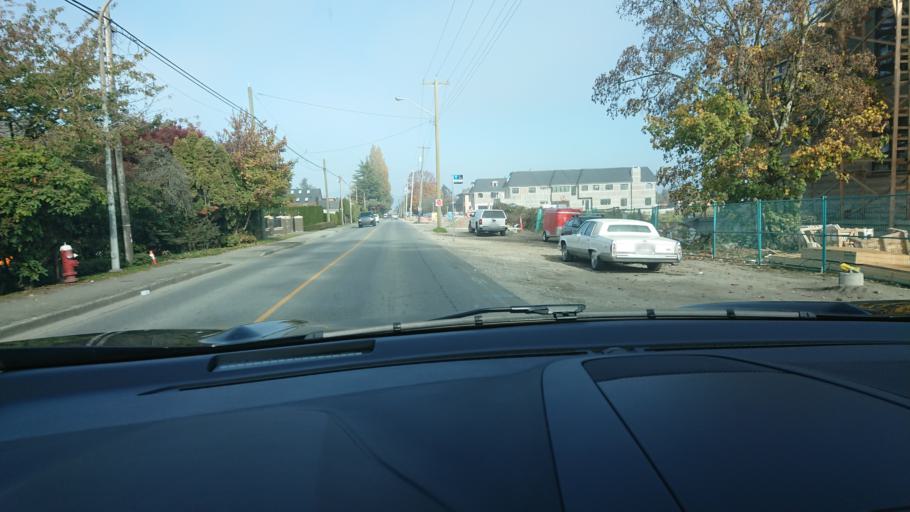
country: CA
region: British Columbia
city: Richmond
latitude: 49.1287
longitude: -123.1589
